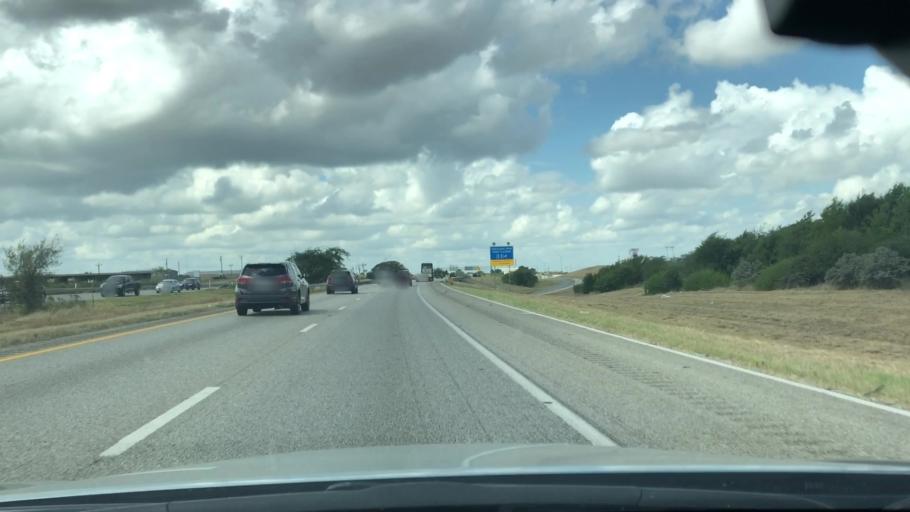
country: US
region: Texas
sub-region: Guadalupe County
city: McQueeney
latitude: 29.5524
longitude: -98.0405
